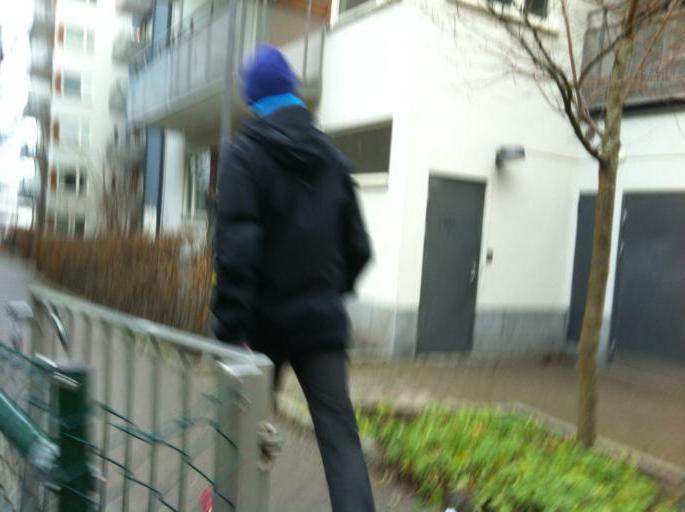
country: SE
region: Stockholm
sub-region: Stockholms Kommun
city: OEstermalm
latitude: 59.3470
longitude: 18.1033
